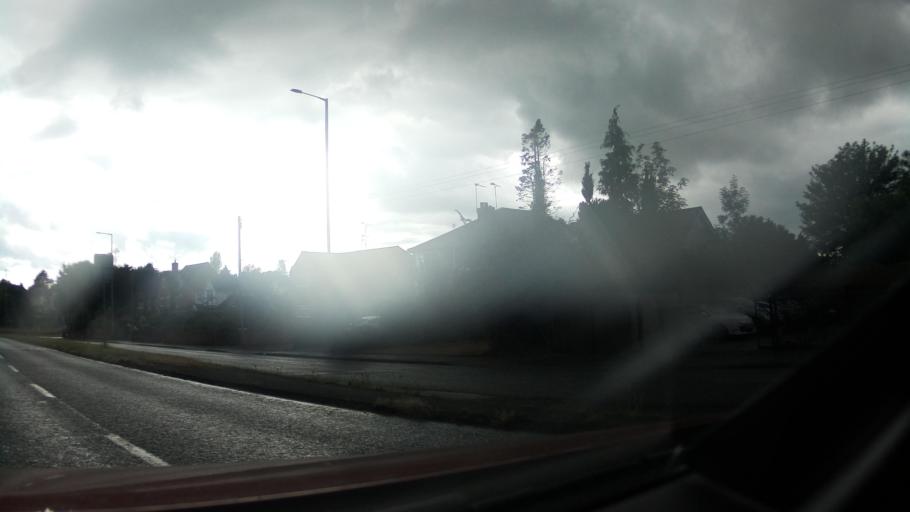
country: GB
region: England
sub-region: Wolverhampton
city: Wolverhampton
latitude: 52.5556
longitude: -2.1707
